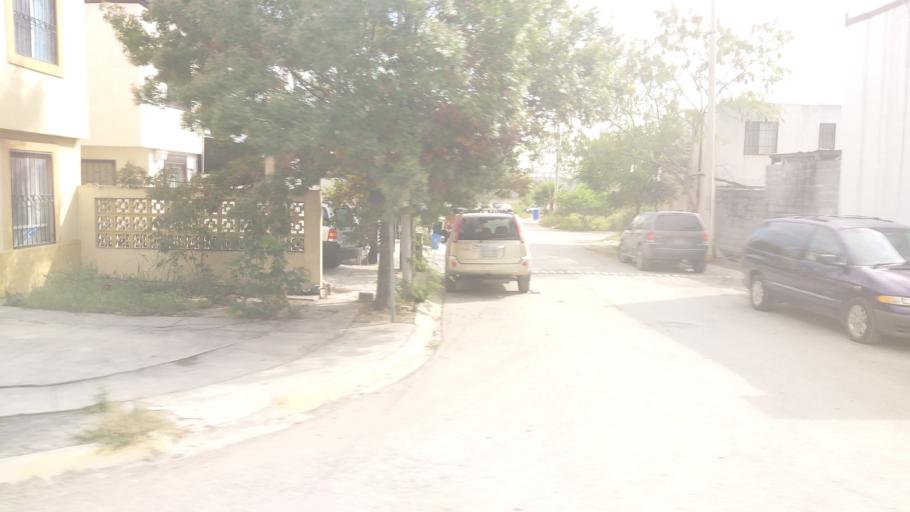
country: MX
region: Nuevo Leon
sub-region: Apodaca
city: Loma la Paz
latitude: 25.7030
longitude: -100.1426
